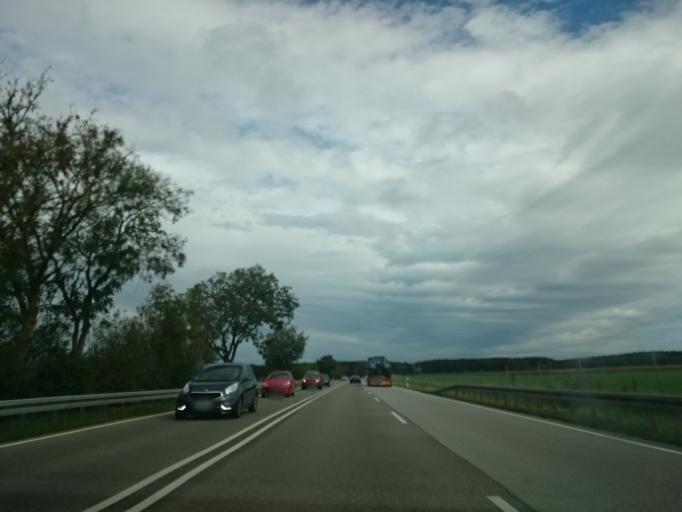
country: DE
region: Bavaria
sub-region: Swabia
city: Rieden
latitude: 47.9734
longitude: 10.6885
